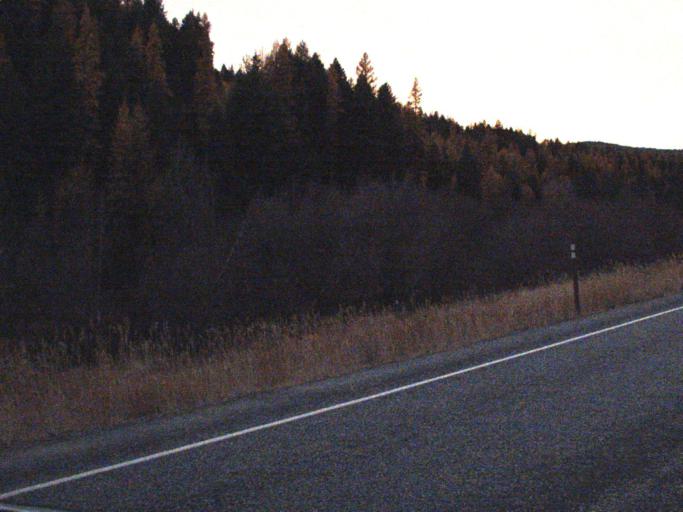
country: US
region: Washington
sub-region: Ferry County
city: Republic
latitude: 48.6498
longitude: -118.7660
